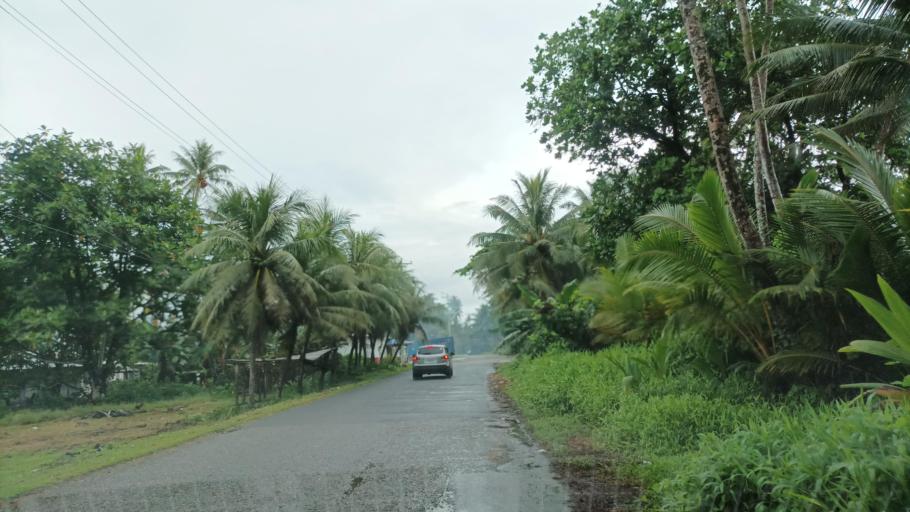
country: FM
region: Kosrae
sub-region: Lelu Municipality
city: Lelu
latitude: 5.3565
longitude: 163.0209
